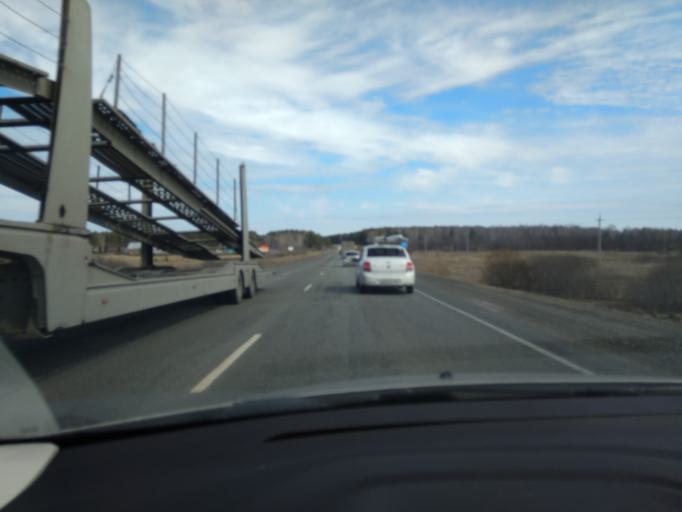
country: RU
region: Sverdlovsk
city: Pyshma
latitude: 57.0463
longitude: 63.4581
